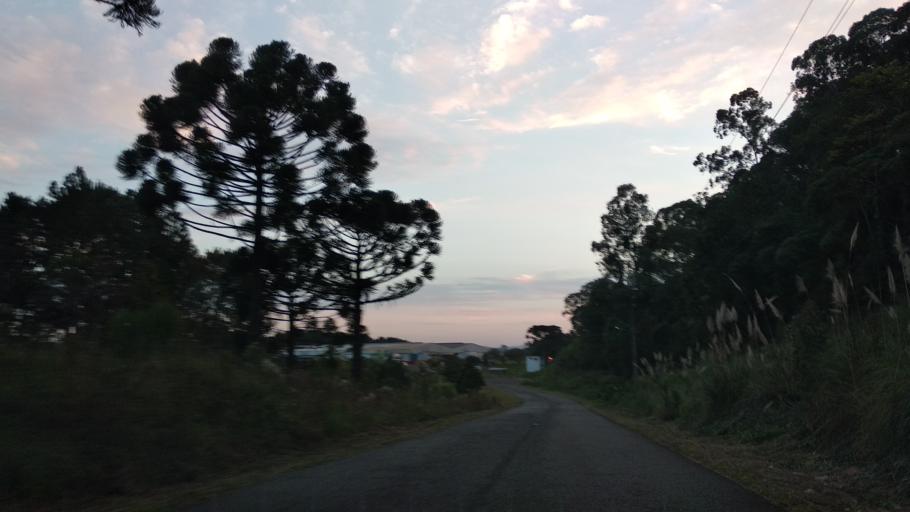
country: BR
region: Santa Catarina
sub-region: Videira
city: Videira
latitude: -26.9974
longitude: -51.1831
